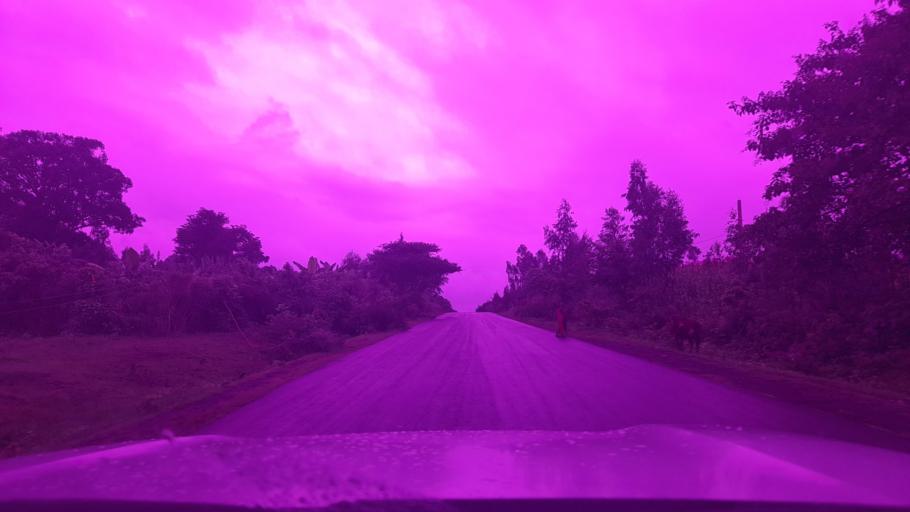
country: ET
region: Oromiya
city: Jima
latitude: 7.8153
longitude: 37.3432
